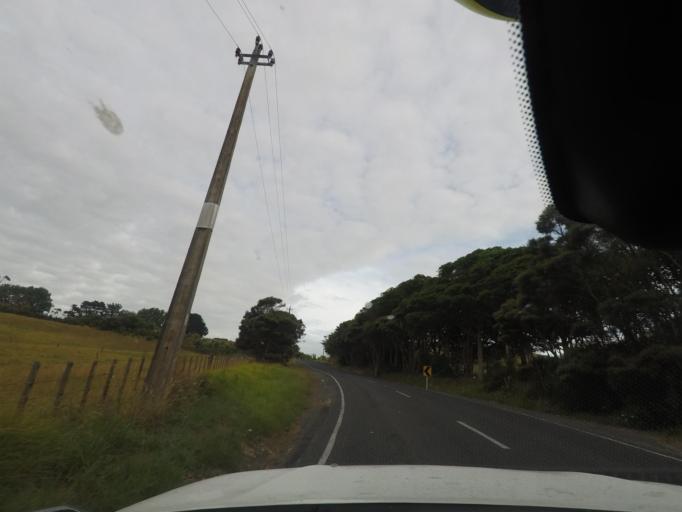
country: NZ
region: Auckland
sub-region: Auckland
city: Parakai
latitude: -36.5294
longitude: 174.2941
